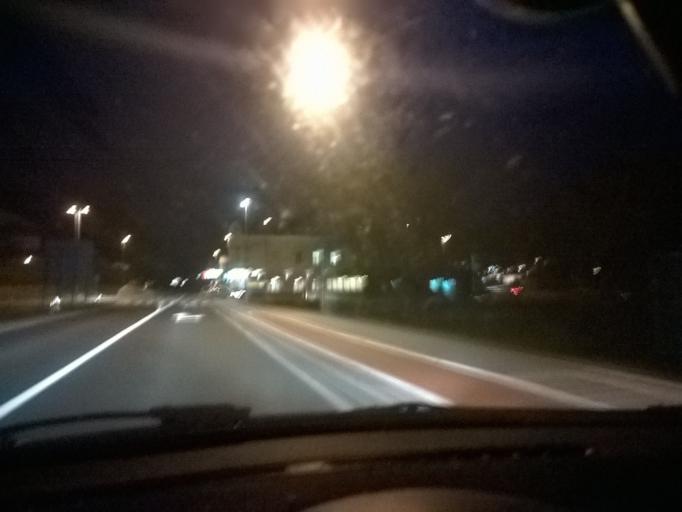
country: SI
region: Rogatec
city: Rogatec
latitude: 46.2245
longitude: 15.7004
